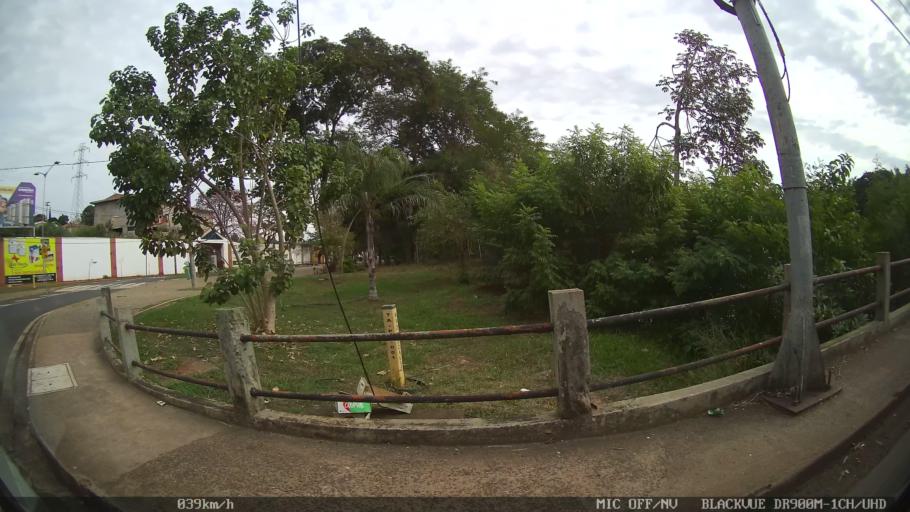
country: BR
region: Sao Paulo
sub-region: Piracicaba
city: Piracicaba
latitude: -22.7060
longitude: -47.6472
